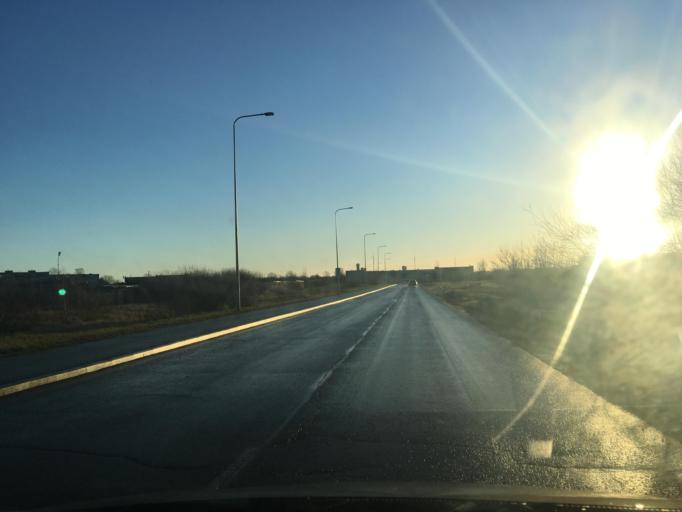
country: EE
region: Ida-Virumaa
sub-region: Narva linn
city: Narva
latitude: 59.3649
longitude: 28.1694
